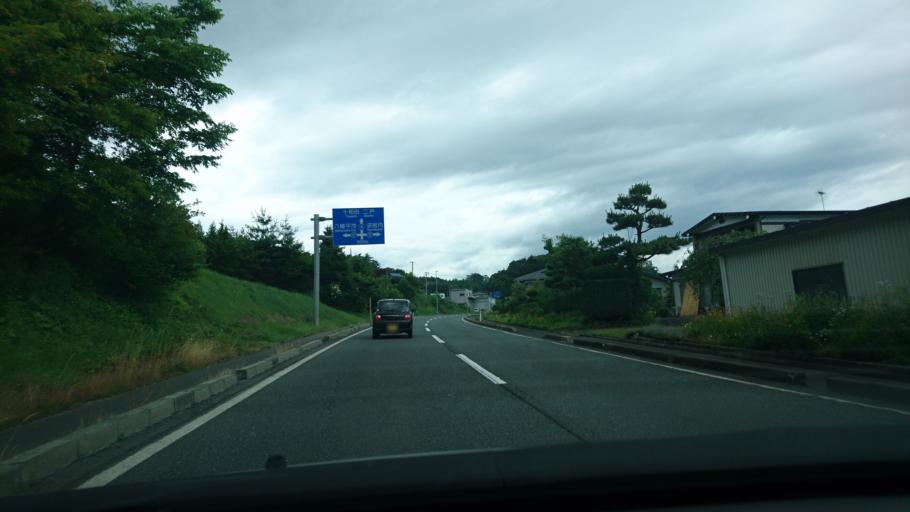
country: JP
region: Iwate
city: Morioka-shi
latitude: 39.9555
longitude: 141.2121
